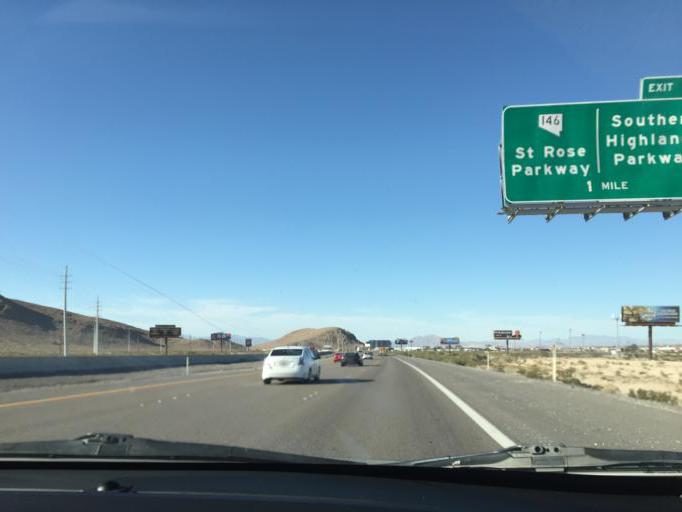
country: US
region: Nevada
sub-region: Clark County
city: Enterprise
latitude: 35.9394
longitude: -115.1866
